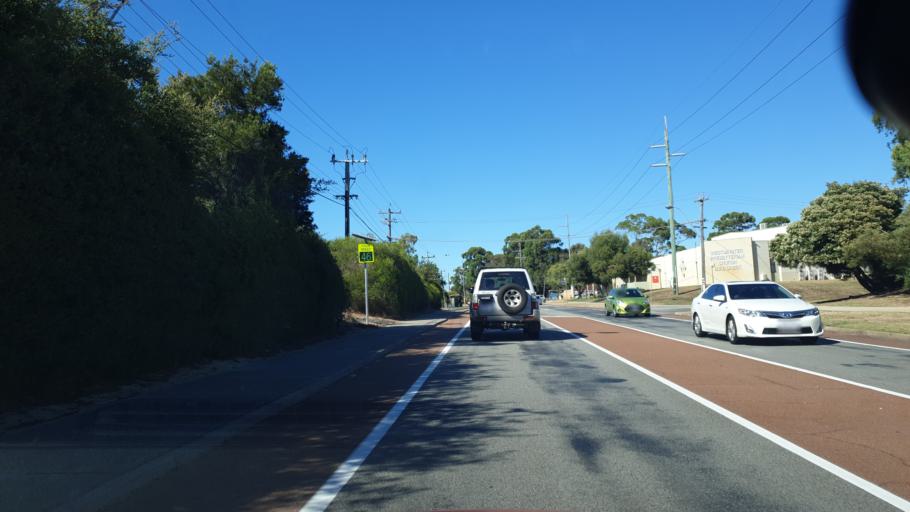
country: AU
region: Western Australia
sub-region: Melville
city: Mount Pleasant
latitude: -32.0510
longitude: 115.8583
